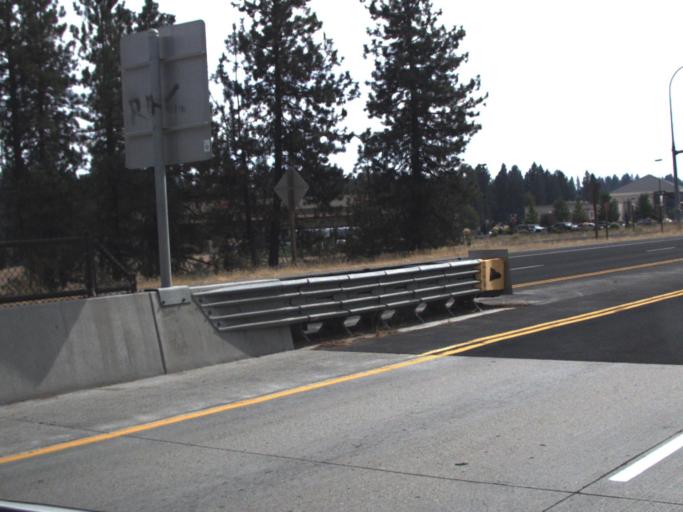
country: US
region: Washington
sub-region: Spokane County
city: Fairwood
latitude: 47.7755
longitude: -117.4025
